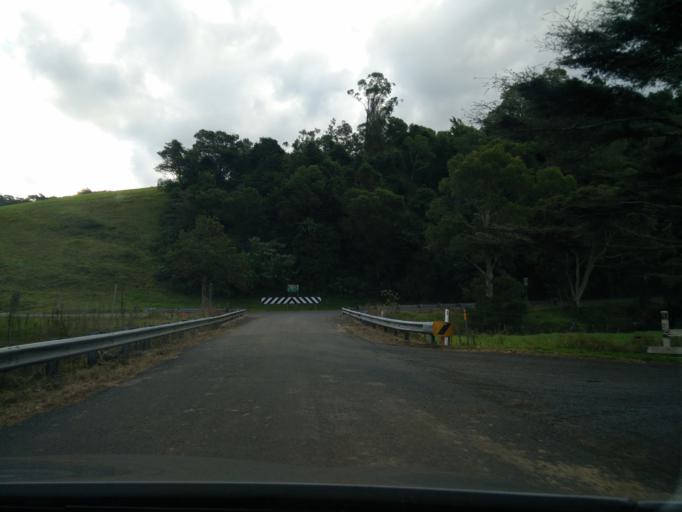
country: AU
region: New South Wales
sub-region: Kiama
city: Jamberoo
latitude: -34.6673
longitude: 150.7905
